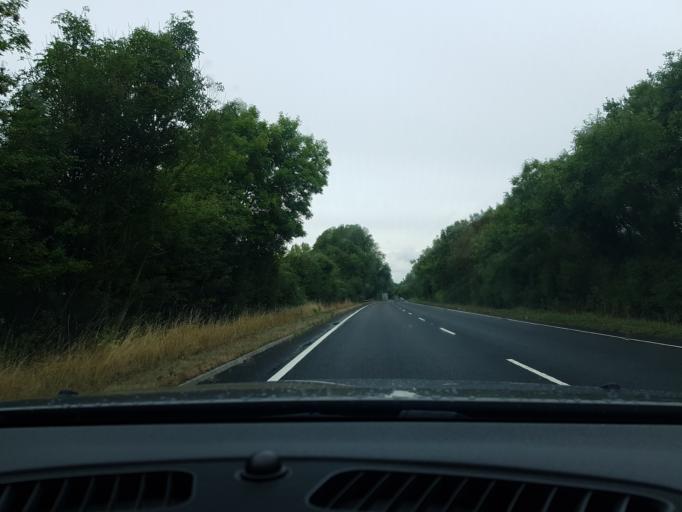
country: GB
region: England
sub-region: Hampshire
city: Odiham
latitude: 51.2646
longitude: -0.9475
